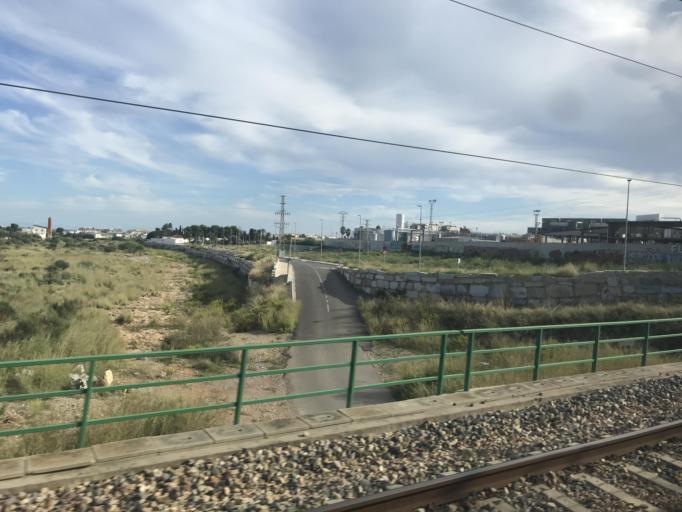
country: ES
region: Valencia
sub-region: Provincia de Castello
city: Benicarlo
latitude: 40.4312
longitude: 0.4181
